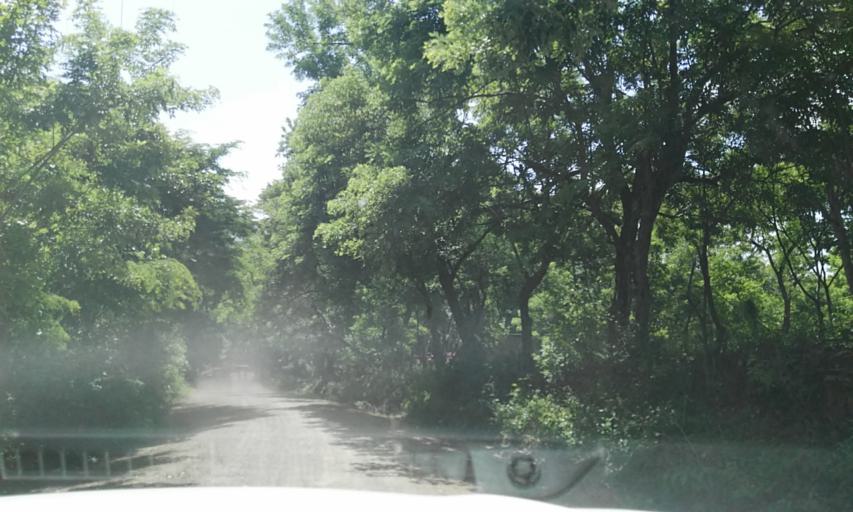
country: NI
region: Matagalpa
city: Terrabona
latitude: 12.6971
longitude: -85.9316
